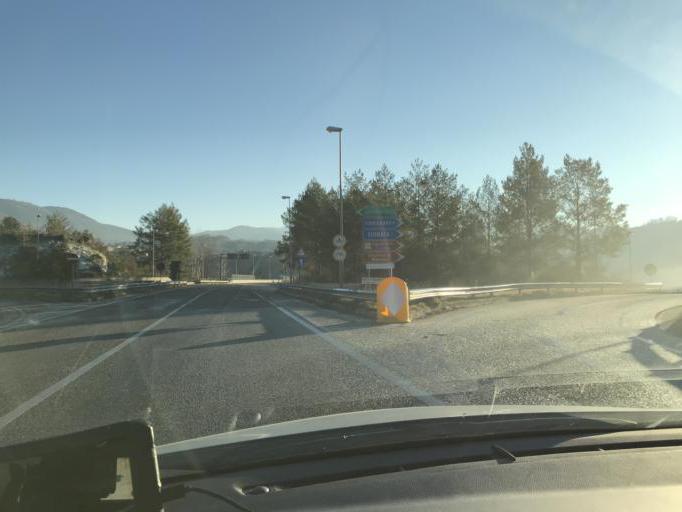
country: IT
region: Latium
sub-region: Provincia di Rieti
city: Fiamignano
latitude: 42.2571
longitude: 13.1304
